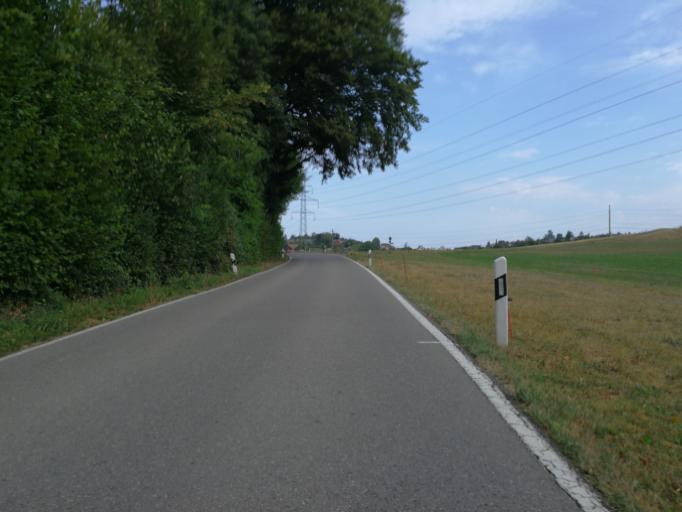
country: CH
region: Zurich
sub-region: Bezirk Hinwil
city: Gossau
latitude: 47.3247
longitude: 8.7630
